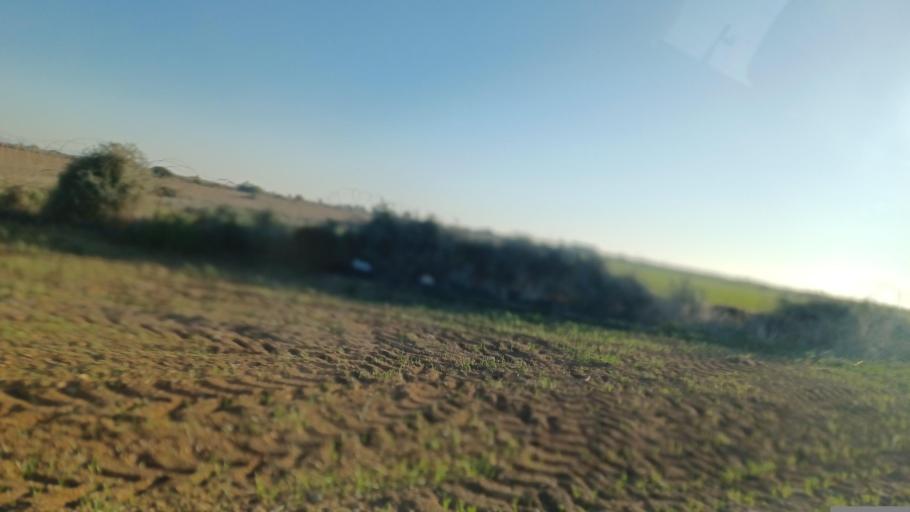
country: CY
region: Lefkosia
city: Kato Deftera
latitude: 35.1472
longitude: 33.2685
